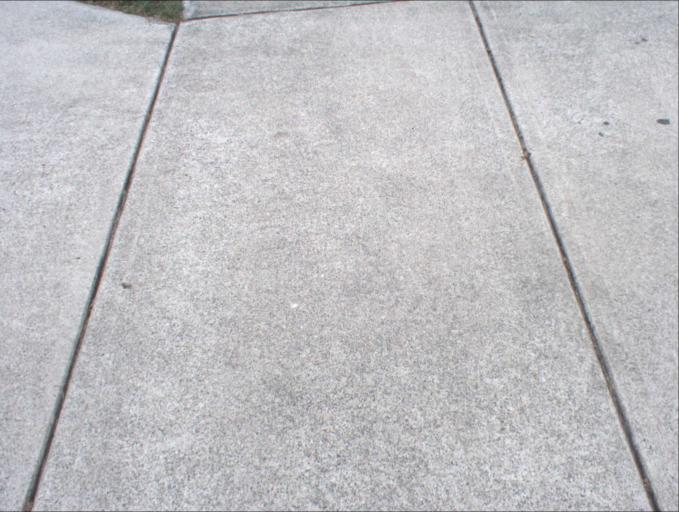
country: AU
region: Queensland
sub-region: Logan
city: Windaroo
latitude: -27.7355
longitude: 153.2074
